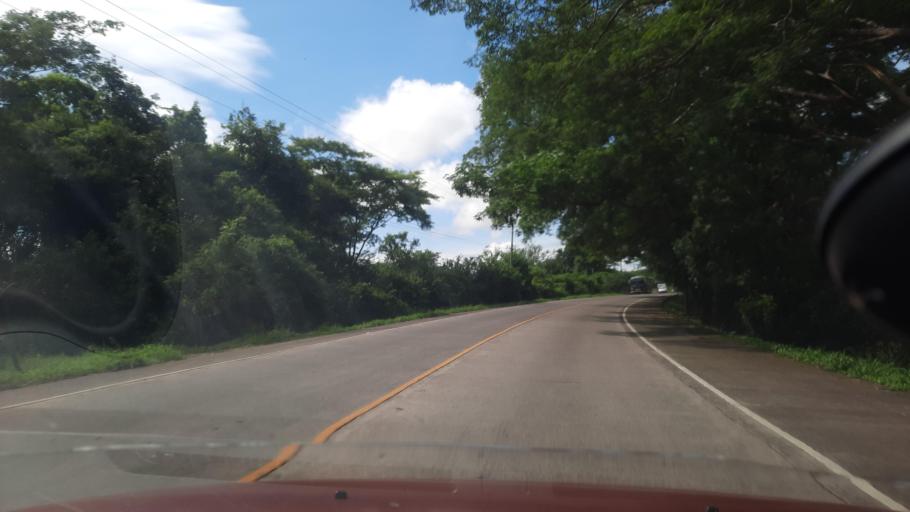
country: SV
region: Usulutan
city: San Agustin
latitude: 13.4413
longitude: -88.7085
